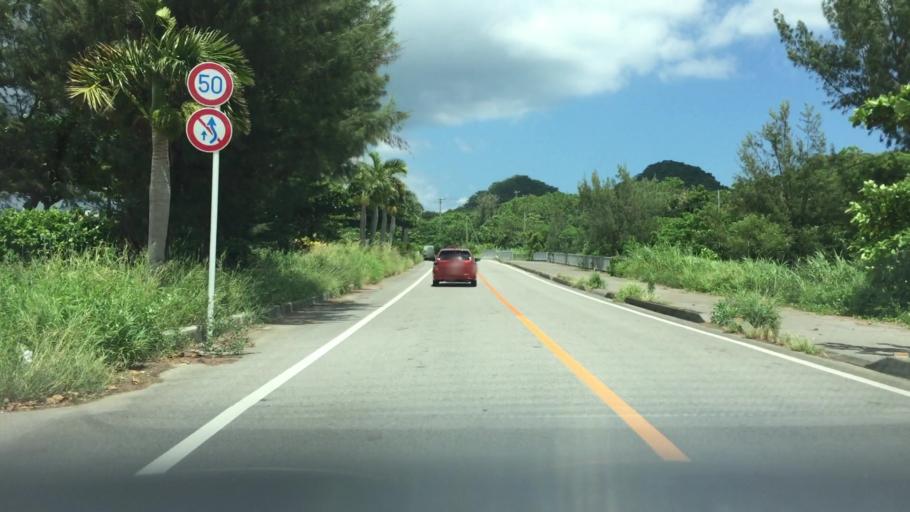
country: JP
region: Okinawa
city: Ishigaki
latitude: 24.4323
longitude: 124.1242
